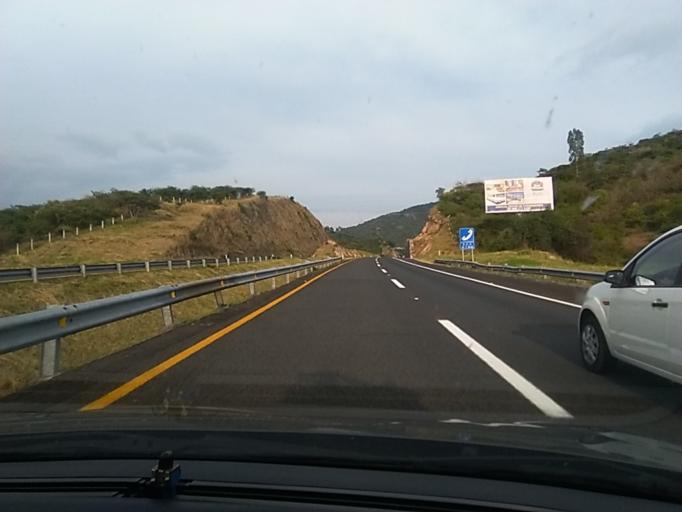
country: MX
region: Michoacan
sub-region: Cuitzeo
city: San Juan Benito Juarez (San Juan Tararameo)
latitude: 19.8930
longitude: -101.1614
